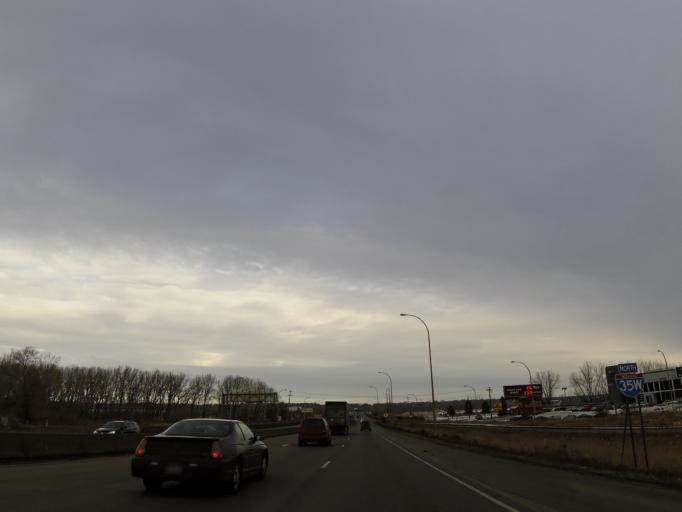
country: US
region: Minnesota
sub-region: Dakota County
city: Burnsville
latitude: 44.7843
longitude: -93.2883
